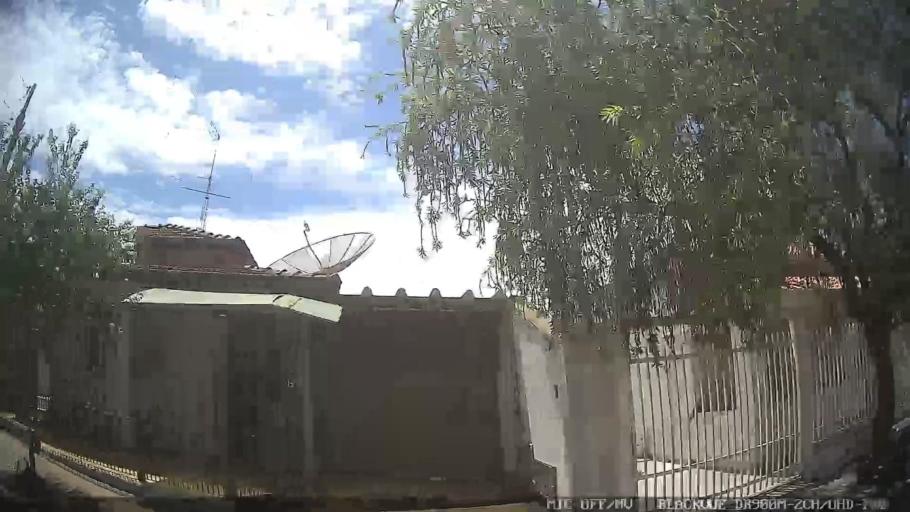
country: BR
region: Sao Paulo
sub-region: Laranjal Paulista
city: Laranjal Paulista
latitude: -23.0423
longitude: -47.8342
